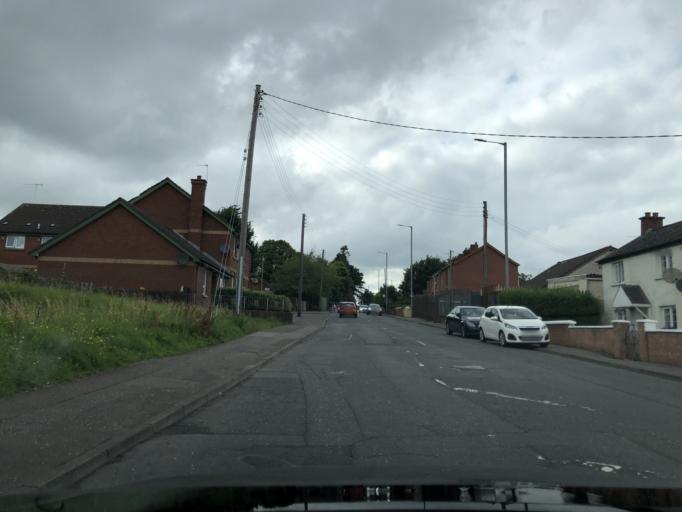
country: GB
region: Northern Ireland
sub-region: Newtownabbey District
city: Newtownabbey
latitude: 54.6533
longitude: -5.9212
